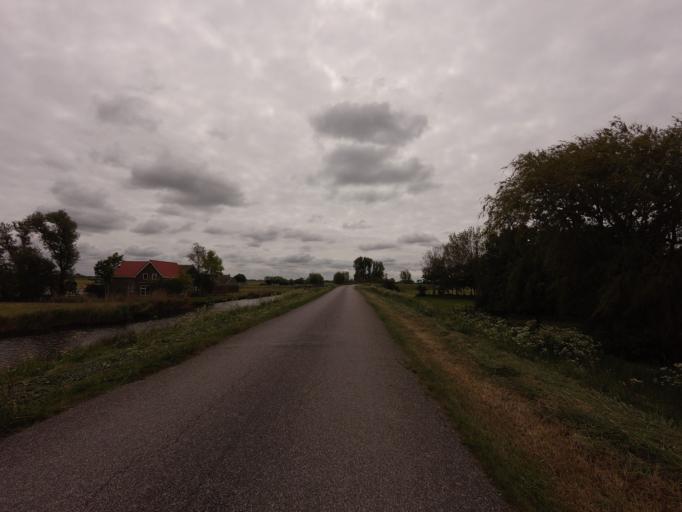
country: NL
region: Friesland
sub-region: Sudwest Fryslan
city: Workum
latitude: 52.9577
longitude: 5.4469
